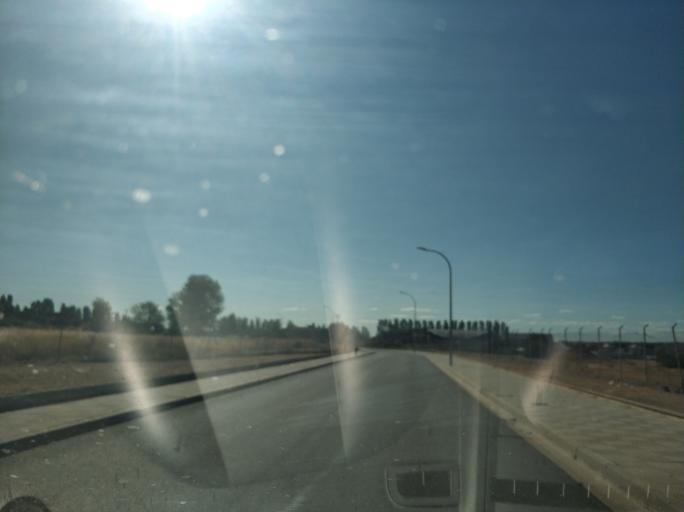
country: ES
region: Castille and Leon
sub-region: Provincia de Salamanca
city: Santa Marta de Tormes
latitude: 40.9451
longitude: -5.6211
